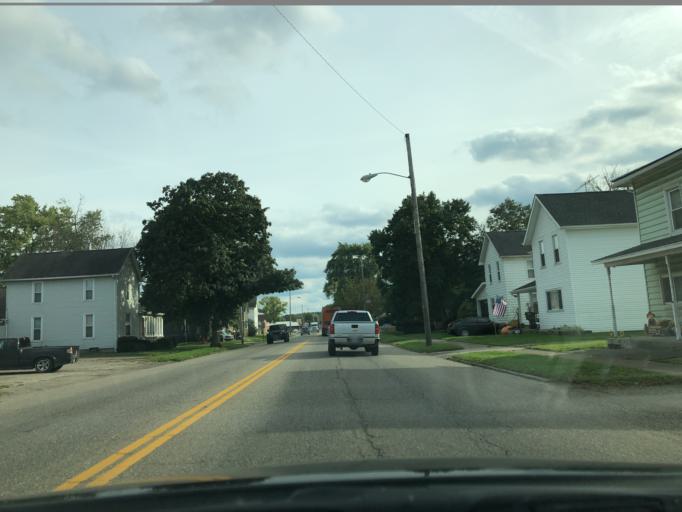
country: US
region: Ohio
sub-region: Tuscarawas County
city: Strasburg
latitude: 40.5962
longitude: -81.5270
